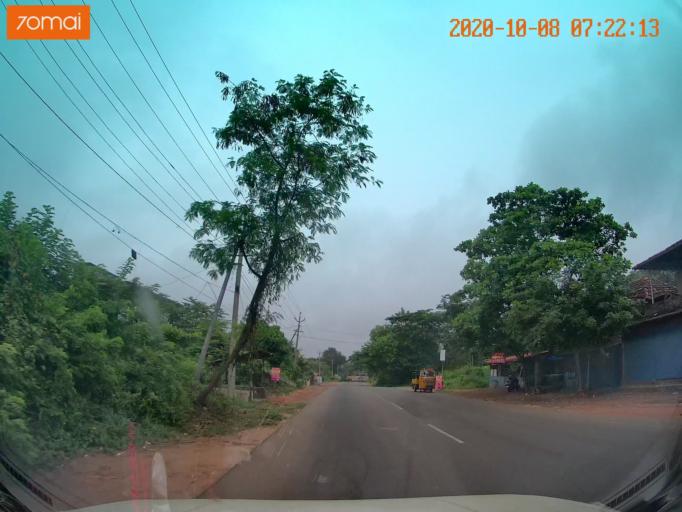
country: IN
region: Kerala
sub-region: Malappuram
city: Tirur
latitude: 10.8621
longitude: 76.0378
